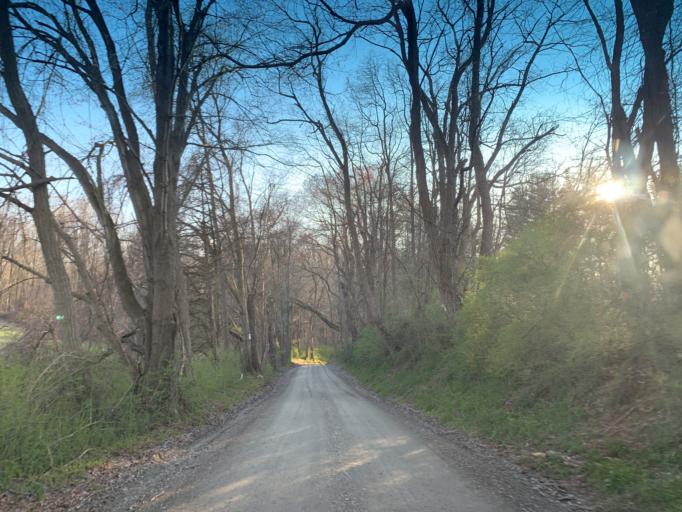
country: US
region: Maryland
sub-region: Harford County
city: South Bel Air
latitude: 39.6034
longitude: -76.2438
